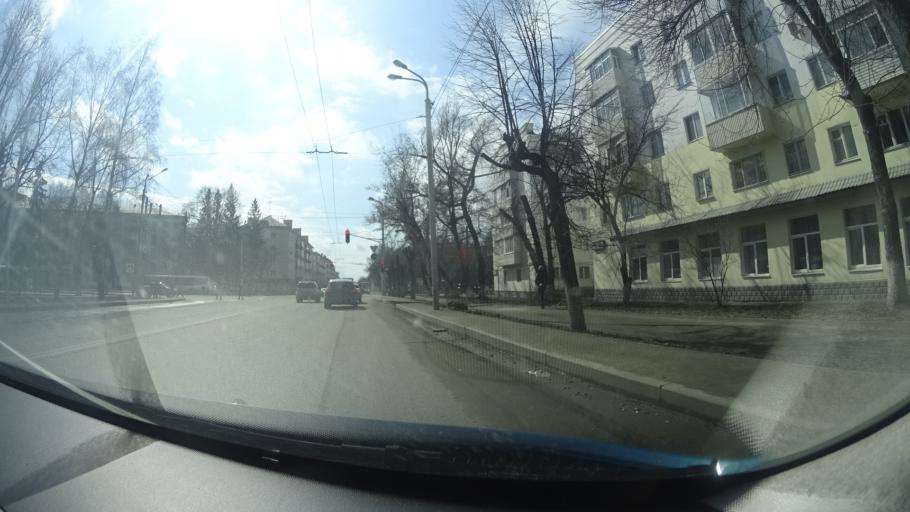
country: RU
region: Bashkortostan
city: Ufa
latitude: 54.7368
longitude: 55.9653
